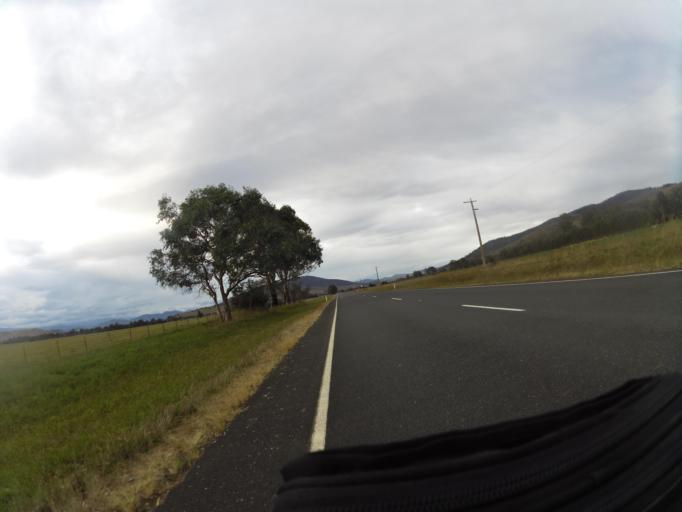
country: AU
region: New South Wales
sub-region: Snowy River
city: Jindabyne
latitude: -36.0962
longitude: 147.9817
